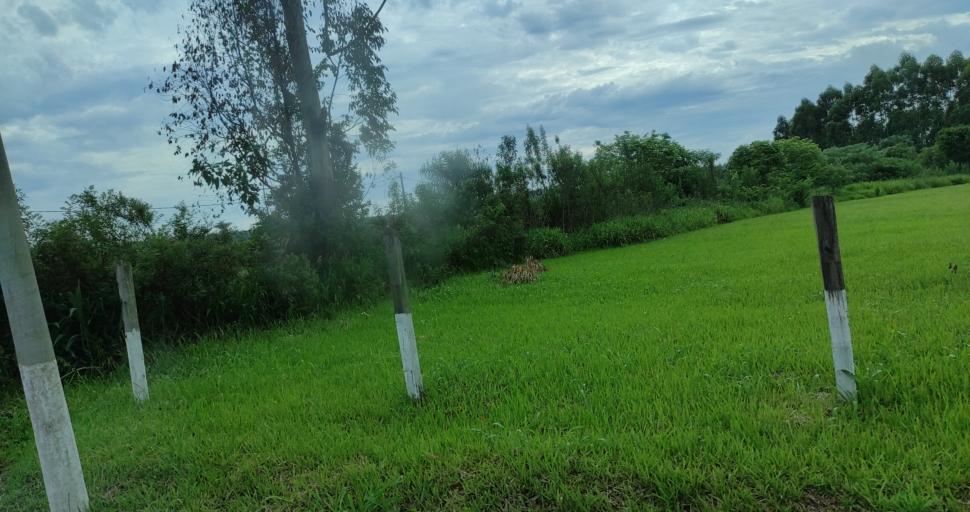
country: AR
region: Misiones
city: Puerto Libertad
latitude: -25.9654
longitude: -54.5937
